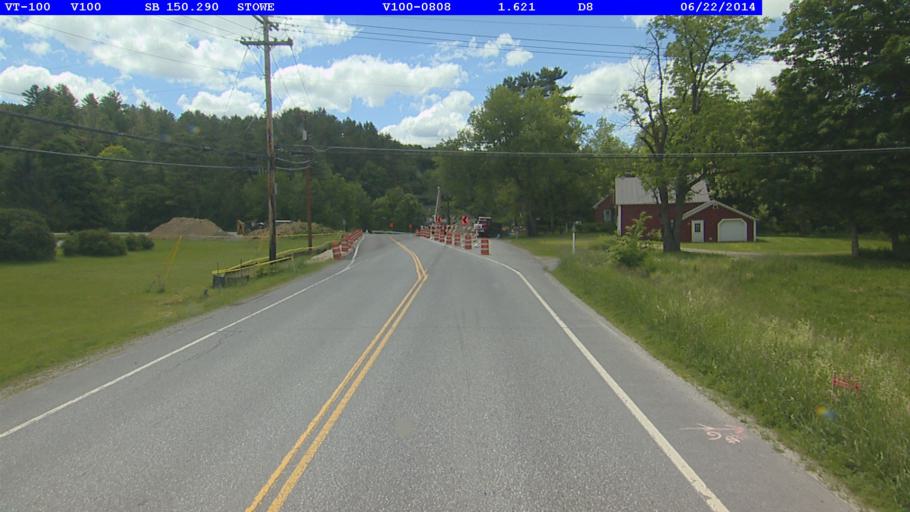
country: US
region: Vermont
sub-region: Washington County
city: Waterbury
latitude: 44.4441
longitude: -72.7025
